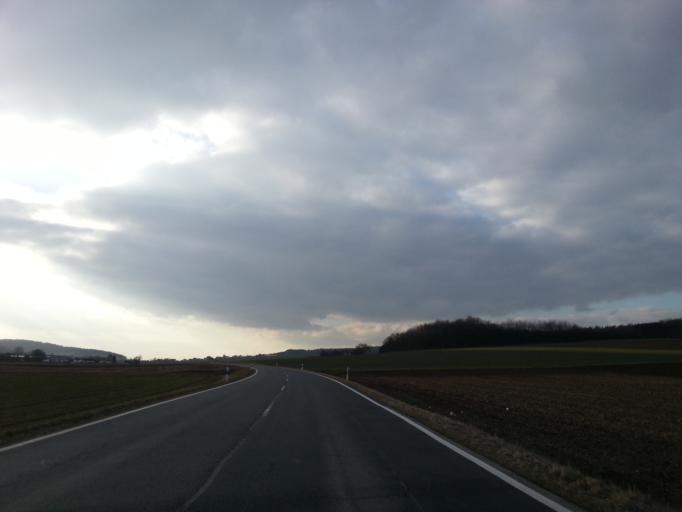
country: DE
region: Bavaria
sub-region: Regierungsbezirk Unterfranken
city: Helmstadt
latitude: 49.7595
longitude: 9.7436
